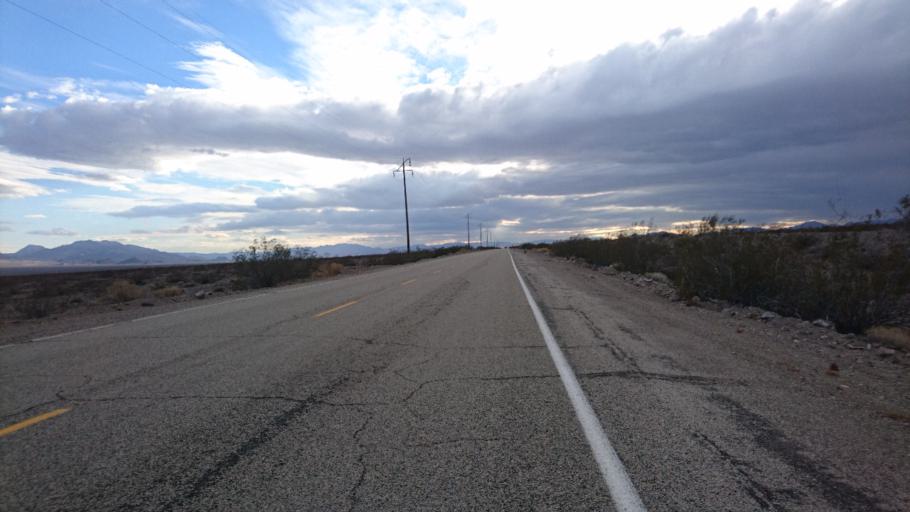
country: US
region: California
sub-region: San Bernardino County
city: Needles
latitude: 34.6595
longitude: -115.3556
